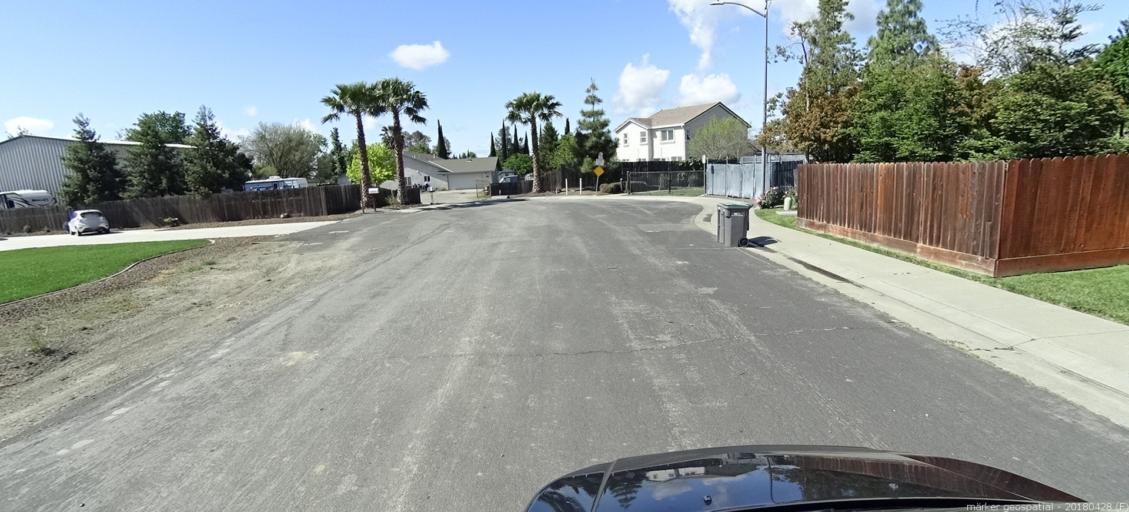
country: US
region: California
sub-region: Yolo County
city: West Sacramento
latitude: 38.5365
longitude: -121.5555
